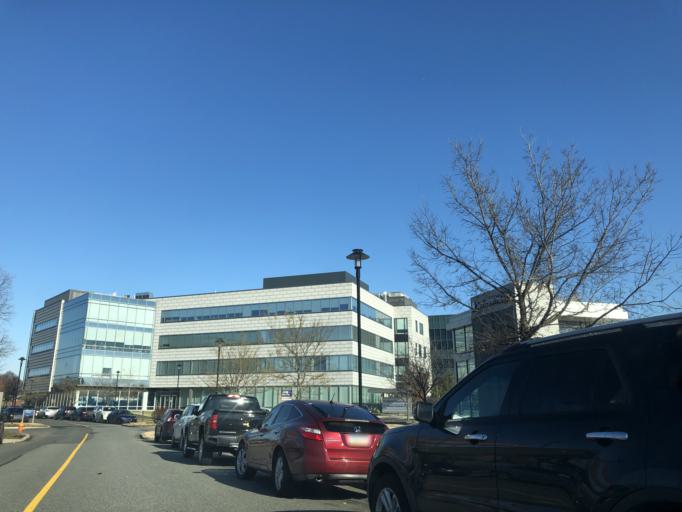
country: US
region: New Jersey
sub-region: Gloucester County
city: National Park
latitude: 39.8949
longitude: -75.1741
